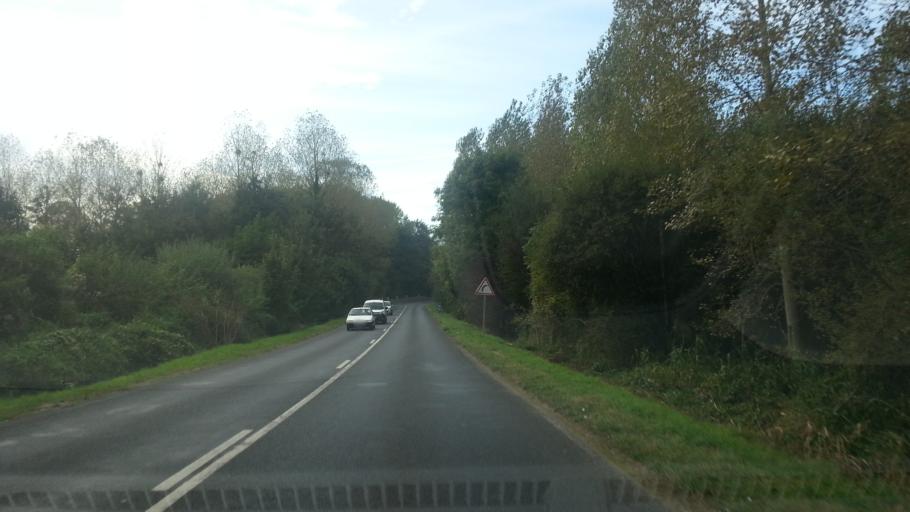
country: FR
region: Picardie
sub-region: Departement de l'Oise
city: Senlis
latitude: 49.2087
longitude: 2.5664
